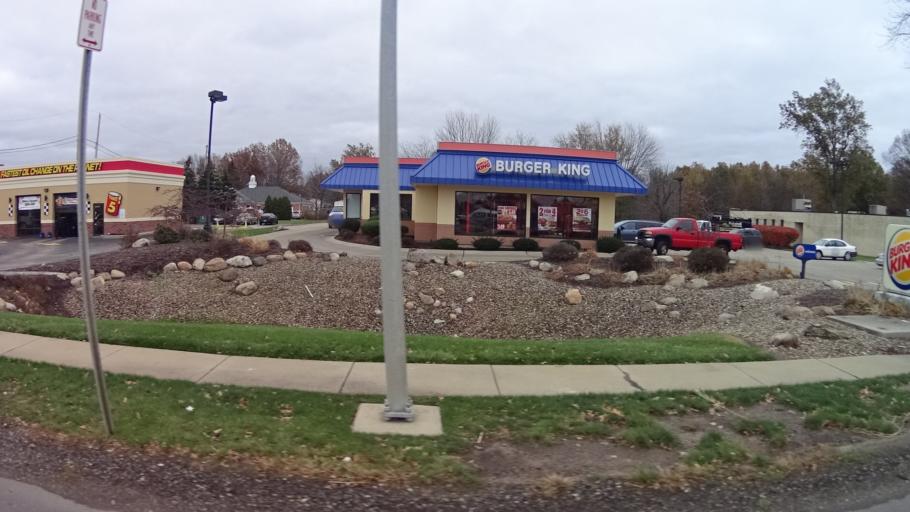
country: US
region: Ohio
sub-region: Lorain County
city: Avon Lake
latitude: 41.4922
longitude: -82.0189
